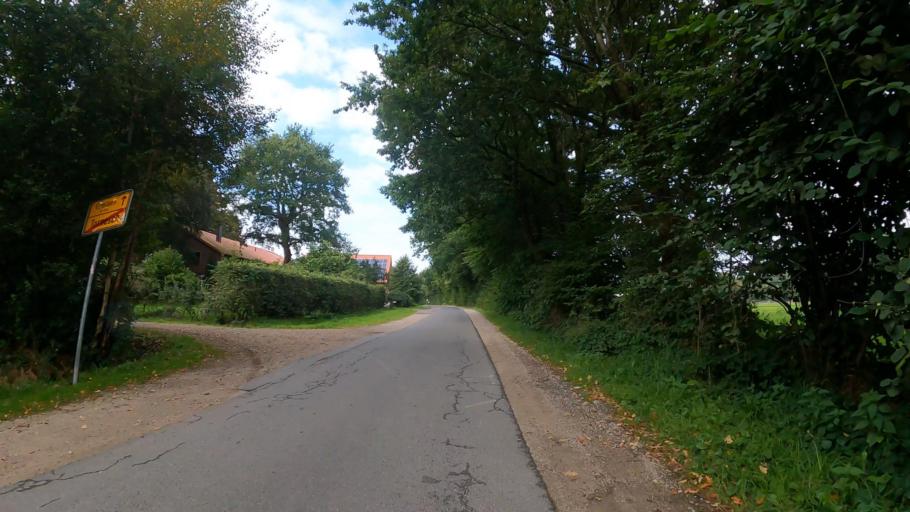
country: DE
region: Schleswig-Holstein
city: Tornesch
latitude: 53.7144
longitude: 9.7109
